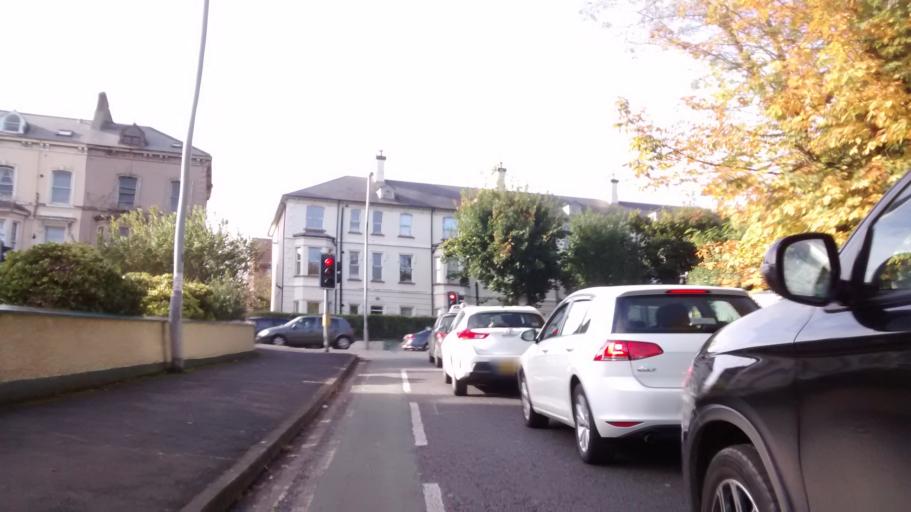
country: GB
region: Northern Ireland
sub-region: City of Derry
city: Derry
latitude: 55.0087
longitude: -7.3252
